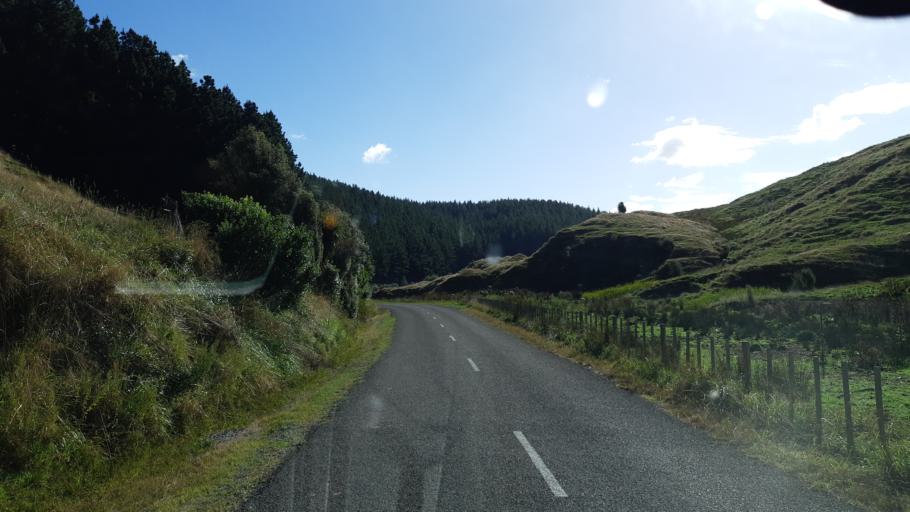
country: NZ
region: Manawatu-Wanganui
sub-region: Rangitikei District
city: Bulls
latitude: -39.9006
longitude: 175.3349
